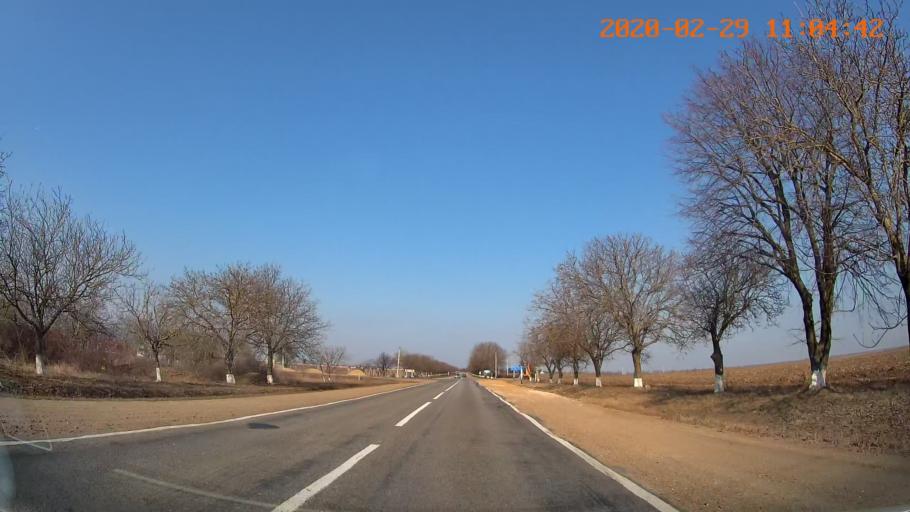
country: MD
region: Criuleni
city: Criuleni
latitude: 47.1927
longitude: 29.1991
